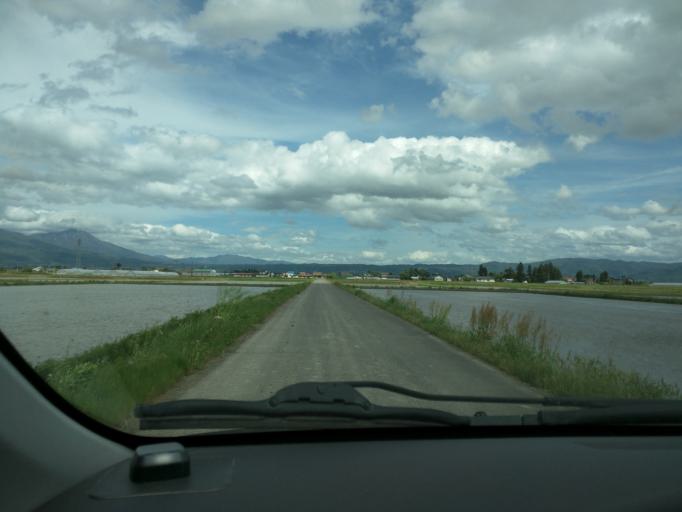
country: JP
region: Fukushima
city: Kitakata
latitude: 37.5456
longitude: 139.8406
